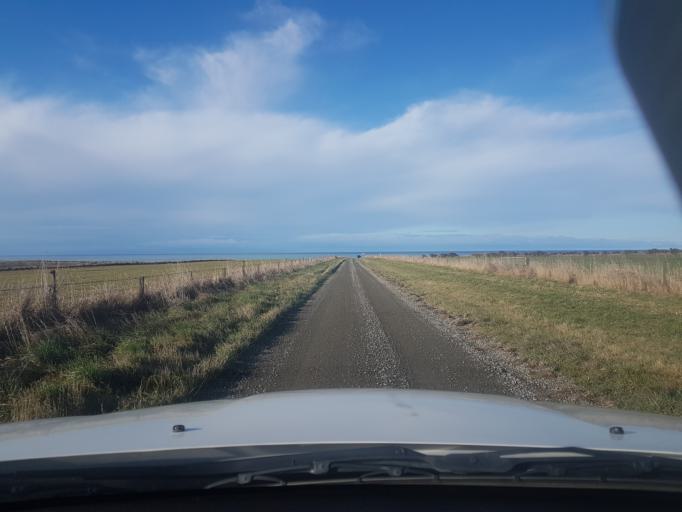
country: NZ
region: Canterbury
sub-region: Timaru District
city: Timaru
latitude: -44.4635
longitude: 171.2398
